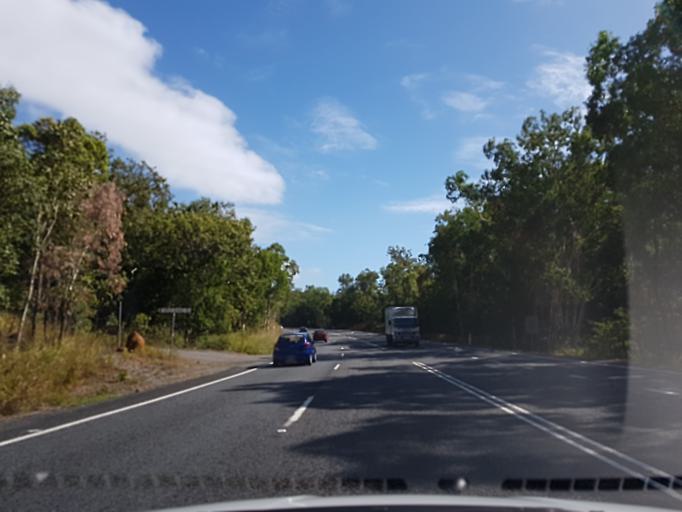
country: AU
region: Queensland
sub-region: Cairns
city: Palm Cove
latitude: -16.6805
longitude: 145.5741
